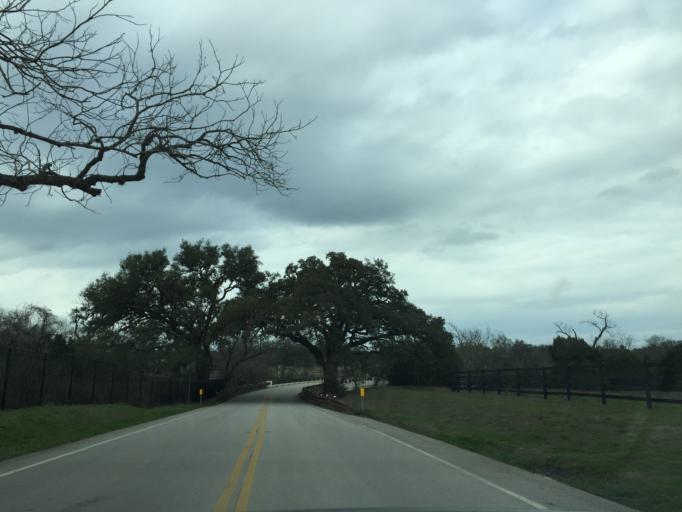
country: US
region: Texas
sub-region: Travis County
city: Shady Hollow
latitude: 30.1508
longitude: -97.9722
